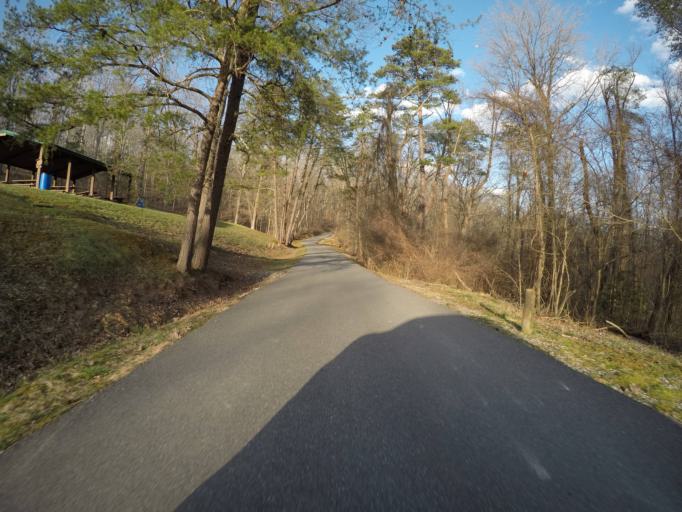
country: US
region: West Virginia
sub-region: Kanawha County
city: Charleston
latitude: 38.3892
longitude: -81.5687
